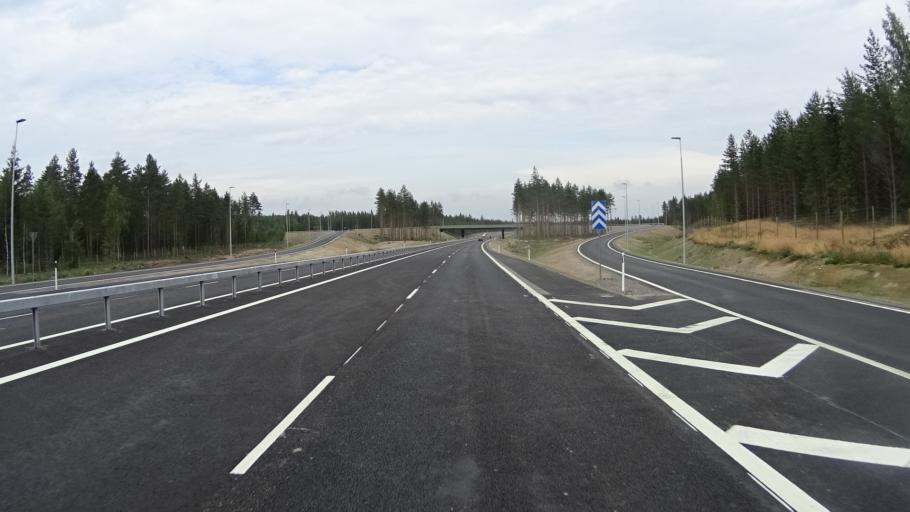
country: FI
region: South Karelia
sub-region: Lappeenranta
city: Lemi
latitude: 60.9731
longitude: 27.8677
